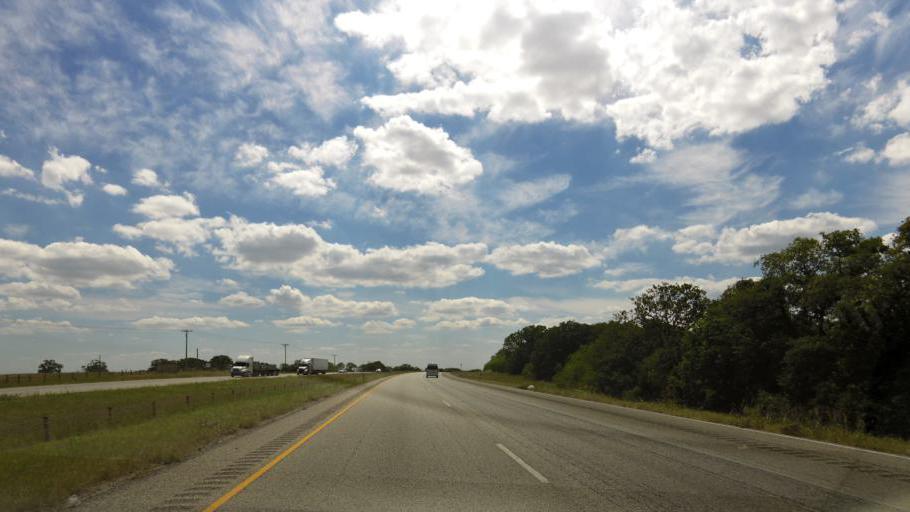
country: US
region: Texas
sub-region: Gonzales County
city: Waelder
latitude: 29.6712
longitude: -97.2927
